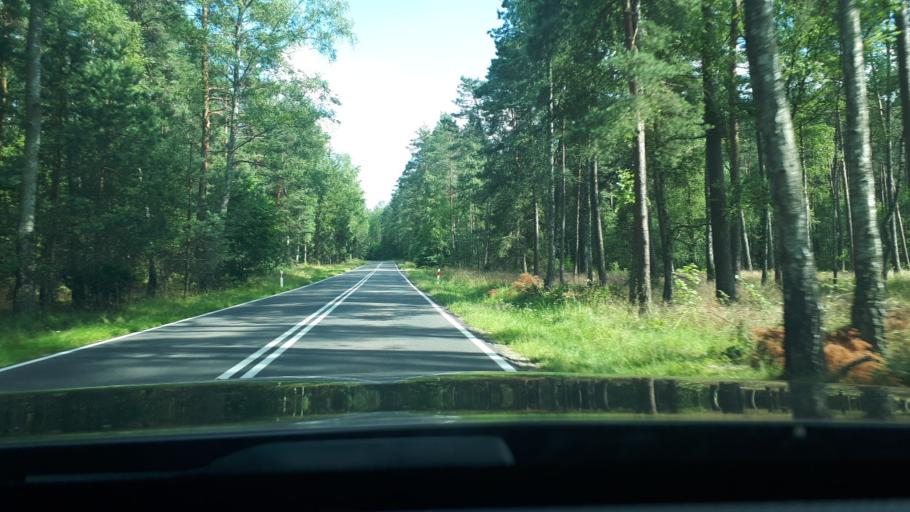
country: PL
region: Warmian-Masurian Voivodeship
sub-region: Powiat olsztynski
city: Stawiguda
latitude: 53.5380
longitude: 20.4262
